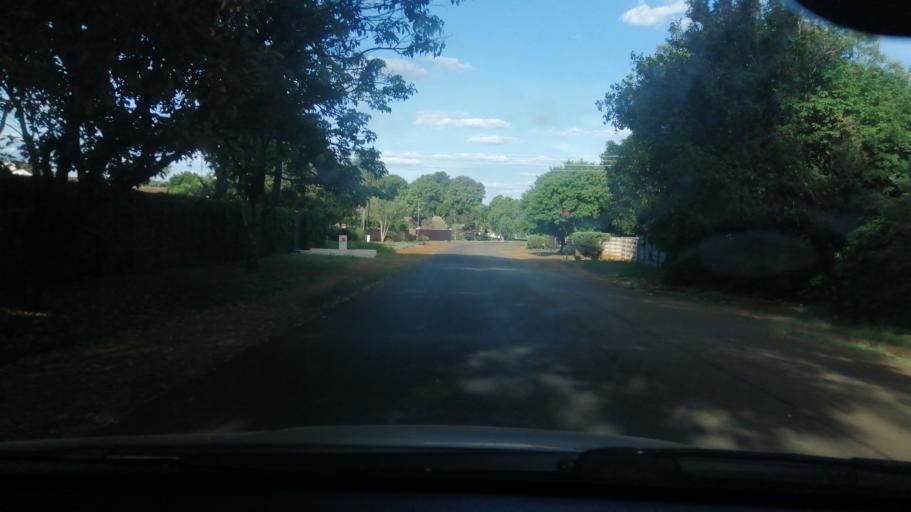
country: ZW
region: Harare
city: Harare
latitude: -17.7644
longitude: 31.0604
